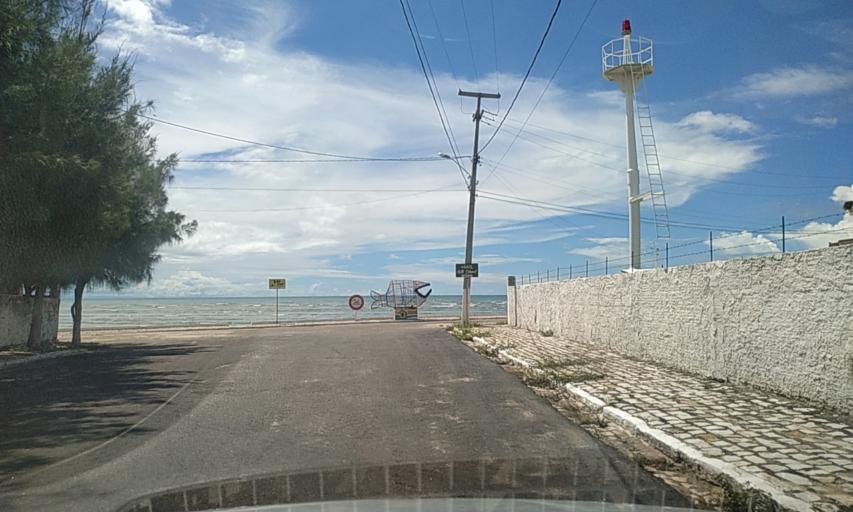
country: BR
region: Rio Grande do Norte
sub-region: Areia Branca
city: Areia Branca
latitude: -4.9272
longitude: -37.1155
